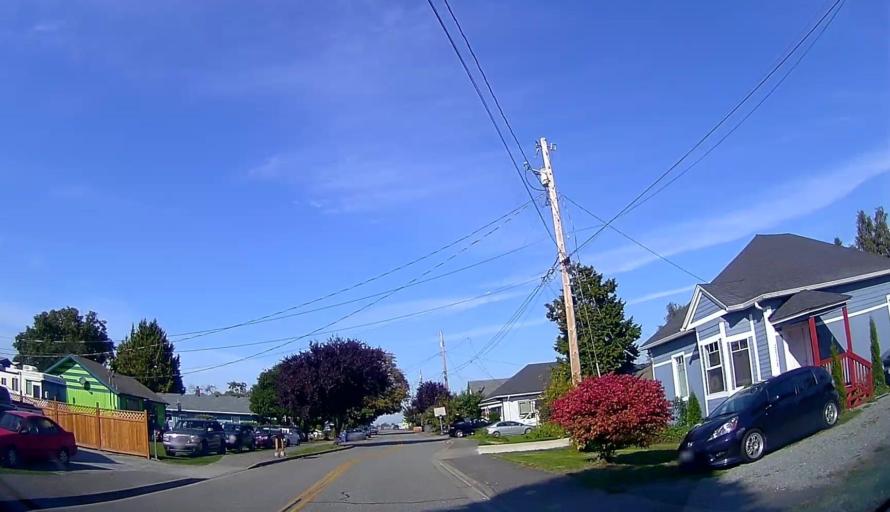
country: US
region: Washington
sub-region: Snohomish County
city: Stanwood
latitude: 48.2426
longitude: -122.3742
